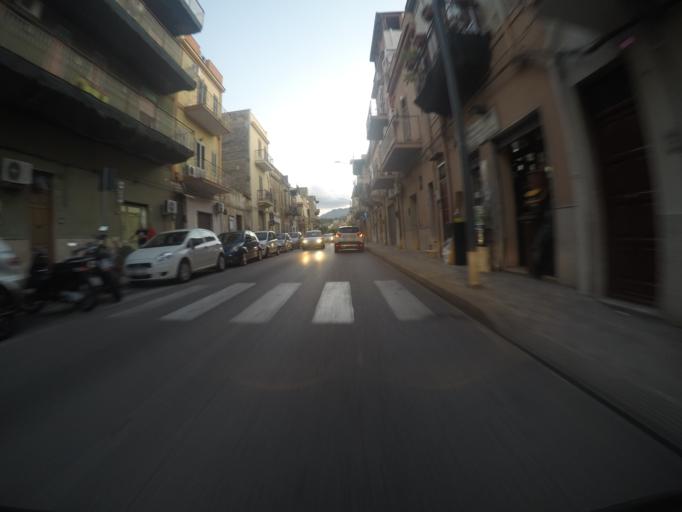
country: IT
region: Sicily
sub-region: Palermo
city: Capaci
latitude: 38.1740
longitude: 13.2410
